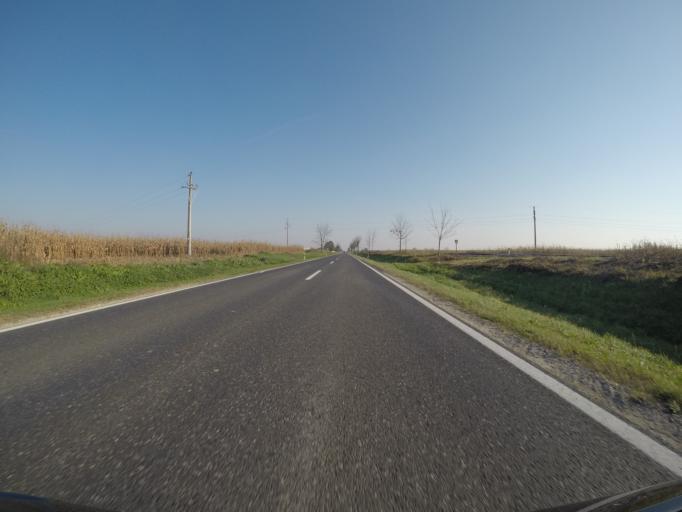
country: HR
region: Koprivnicko-Krizevacka
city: Kalinovac
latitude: 46.0165
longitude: 17.0906
